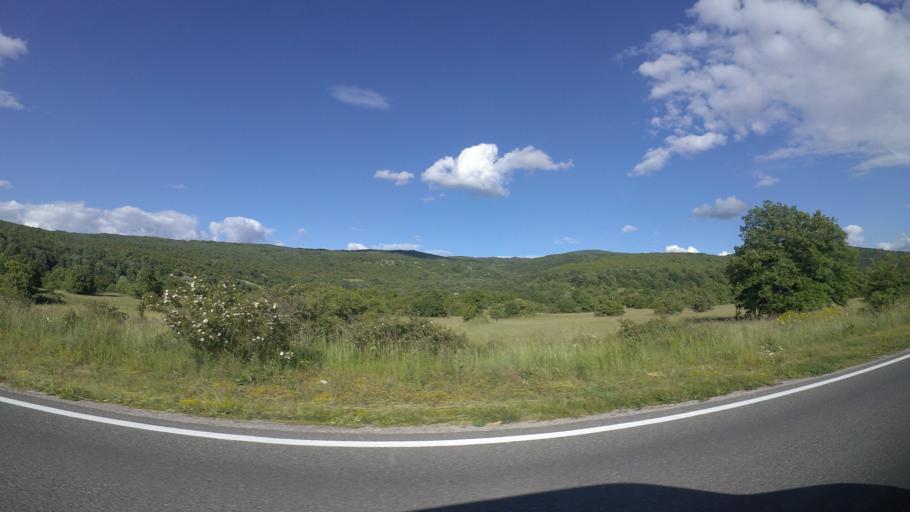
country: BA
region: Federation of Bosnia and Herzegovina
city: Bihac
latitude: 44.6508
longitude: 15.7186
